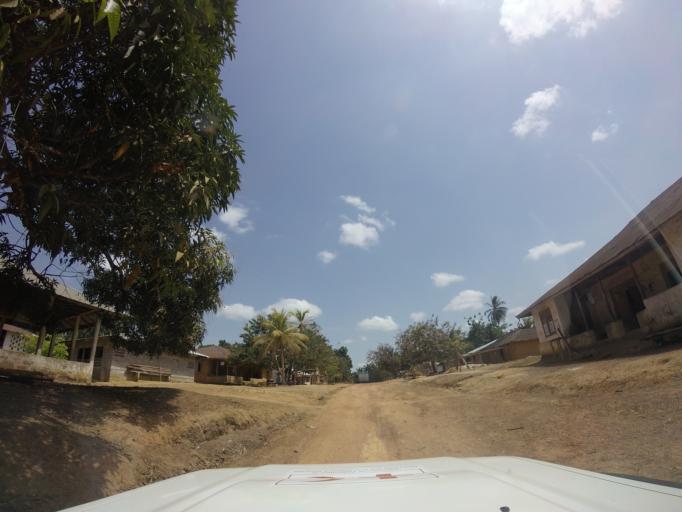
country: SL
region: Southern Province
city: Zimmi
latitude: 7.0449
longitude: -11.2819
